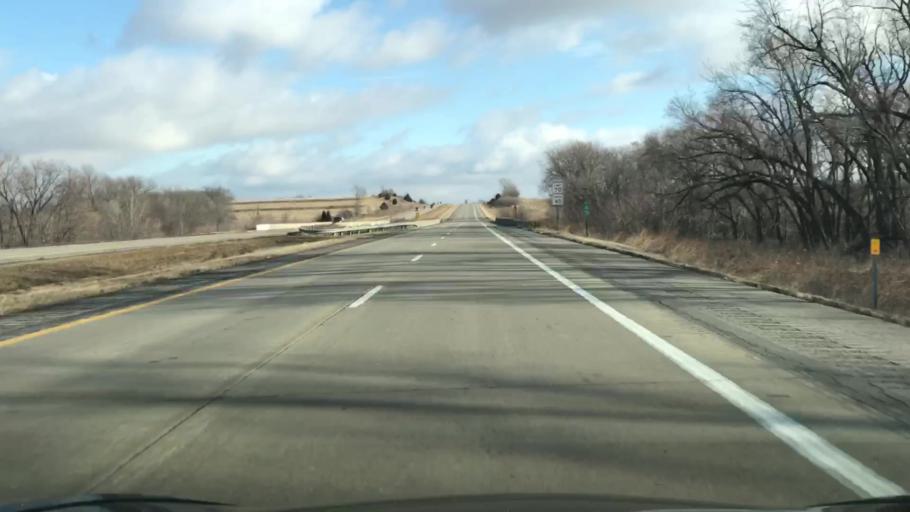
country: US
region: Iowa
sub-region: Cass County
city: Atlantic
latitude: 41.4972
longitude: -94.8608
